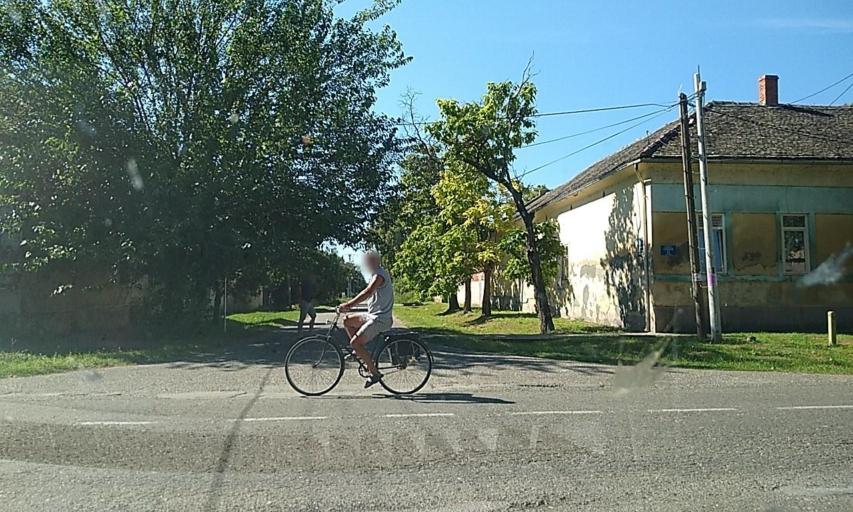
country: RS
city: Backo Gradiste
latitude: 45.5338
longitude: 20.0263
